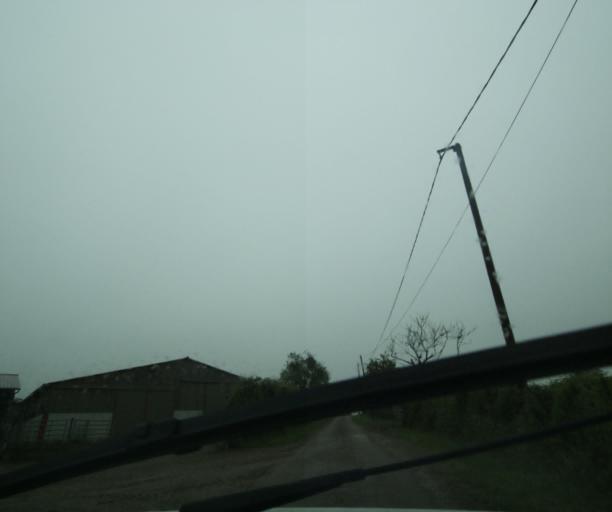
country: FR
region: Bourgogne
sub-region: Departement de Saone-et-Loire
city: Charolles
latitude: 46.3920
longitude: 4.2321
